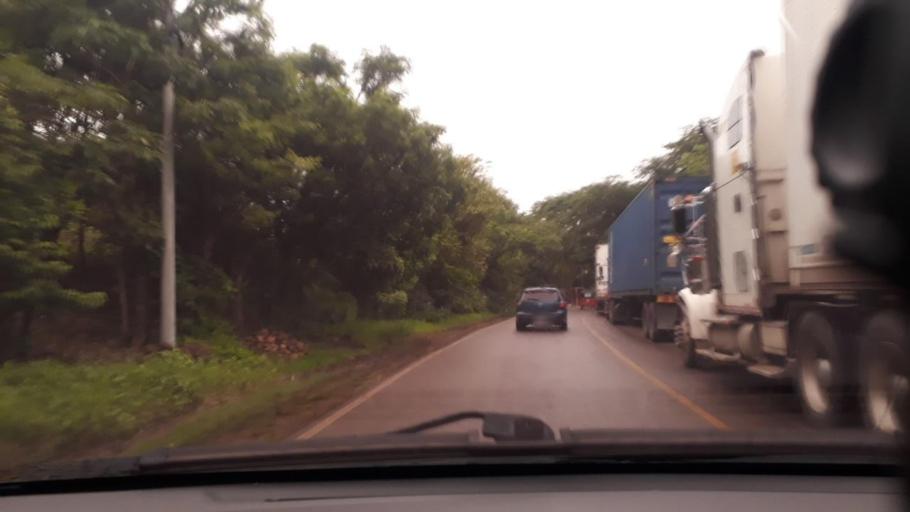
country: GT
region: Jutiapa
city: Atescatempa
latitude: 14.2009
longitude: -89.6794
